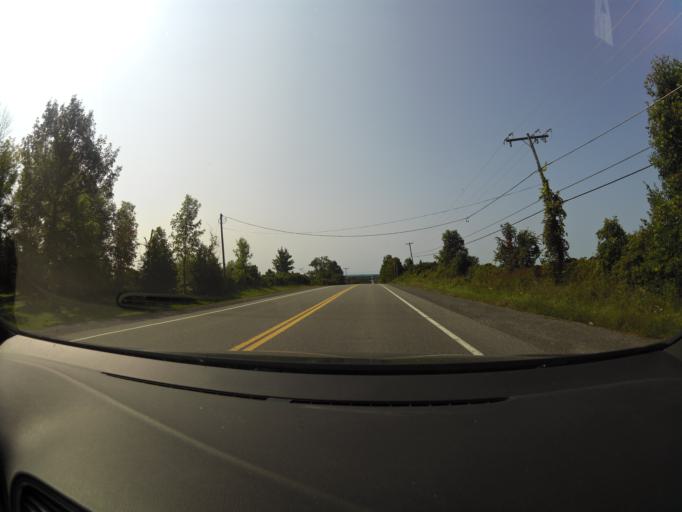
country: CA
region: Ontario
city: Arnprior
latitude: 45.4712
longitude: -76.1795
